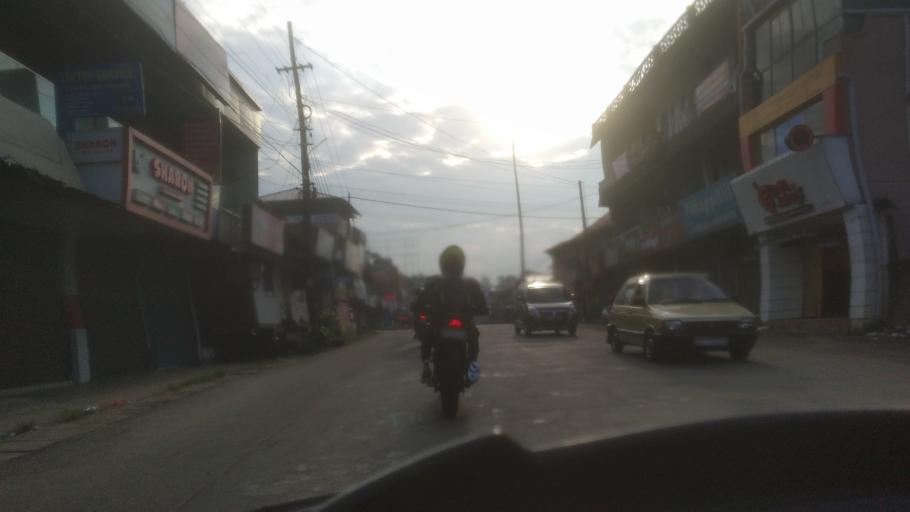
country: IN
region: Kerala
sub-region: Ernakulam
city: Perumpavur
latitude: 10.1125
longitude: 76.5177
